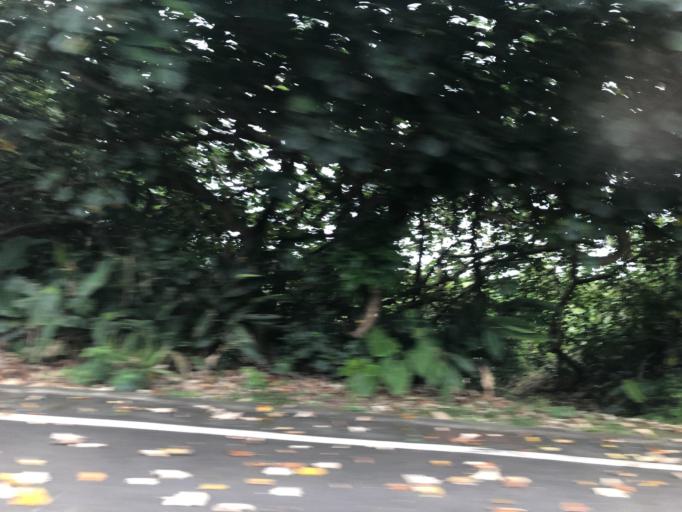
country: TW
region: Taiwan
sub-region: Keelung
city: Keelung
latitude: 25.2182
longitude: 121.6481
